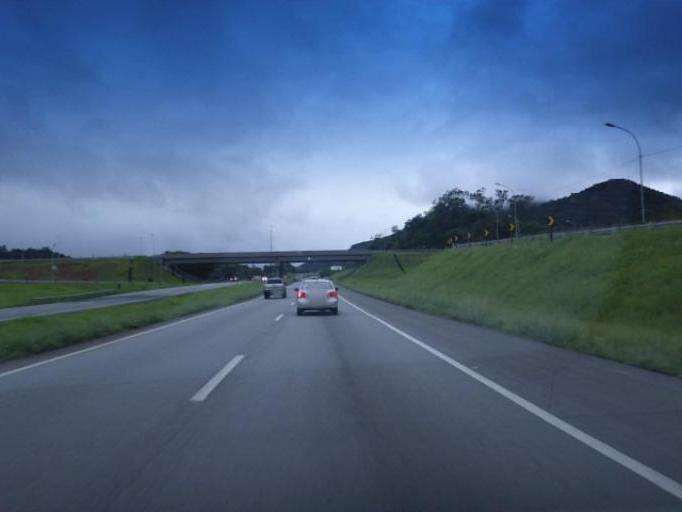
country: BR
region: Sao Paulo
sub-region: Miracatu
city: Miracatu
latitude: -24.3138
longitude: -47.5193
